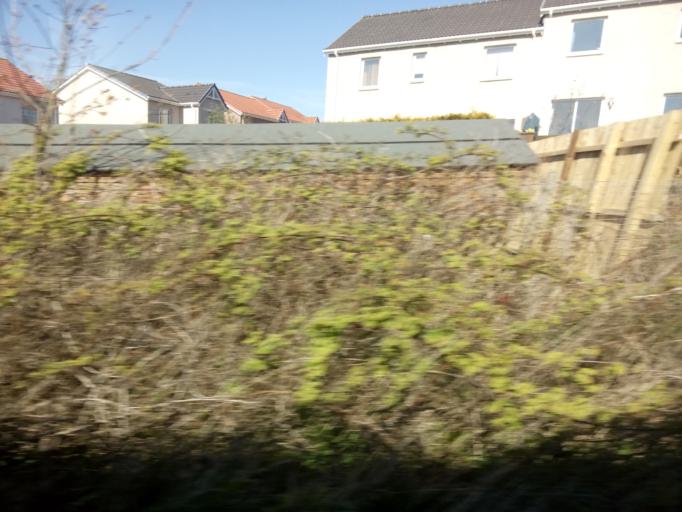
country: GB
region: Scotland
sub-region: Fife
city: Kirkcaldy
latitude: 56.1280
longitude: -3.1253
